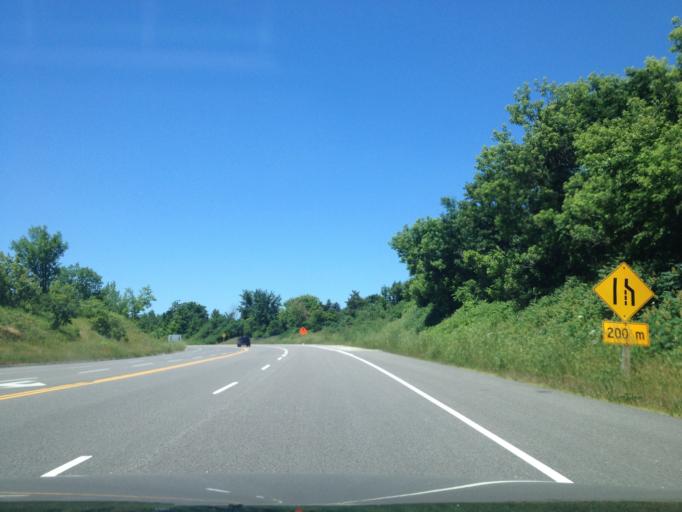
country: CA
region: Ontario
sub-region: Halton
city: Milton
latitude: 43.6730
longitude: -79.9828
